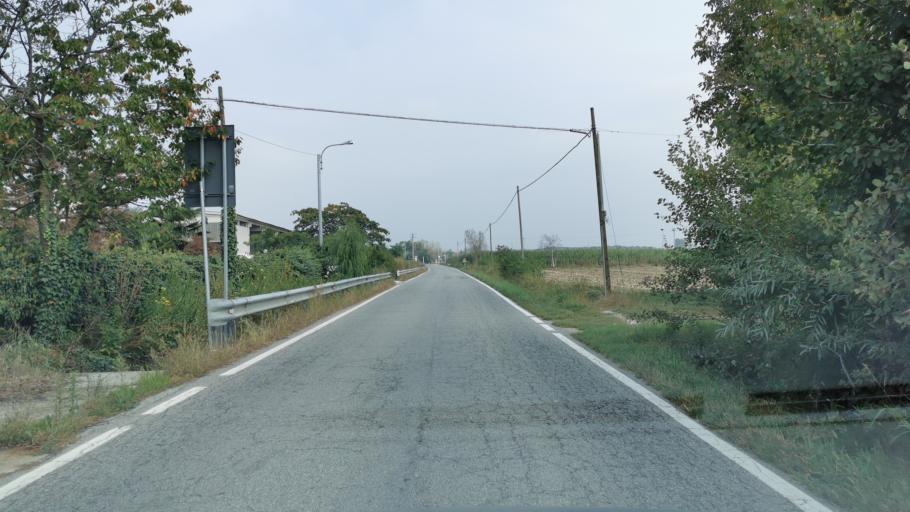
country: IT
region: Piedmont
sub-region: Provincia di Torino
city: Rondissone
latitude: 45.2401
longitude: 7.9169
